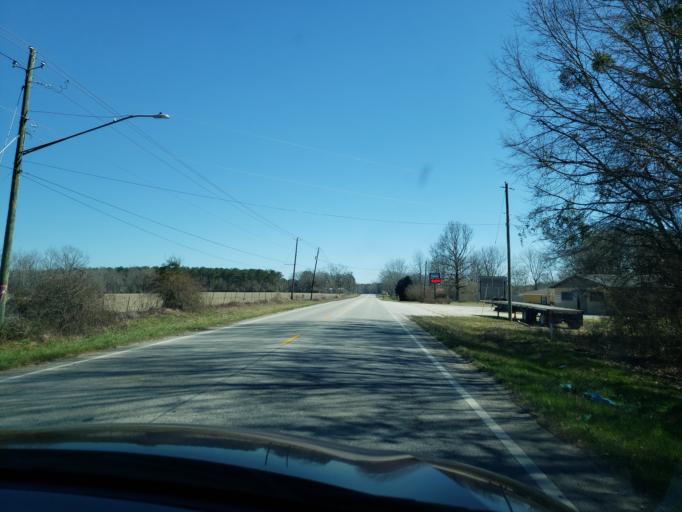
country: US
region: Alabama
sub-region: Lee County
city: Auburn
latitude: 32.6024
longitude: -85.5856
